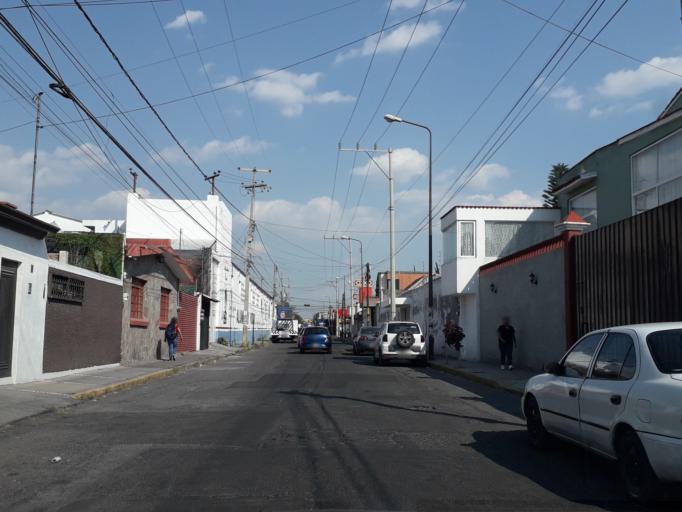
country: MX
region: Puebla
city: Puebla
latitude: 19.0169
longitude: -98.2136
